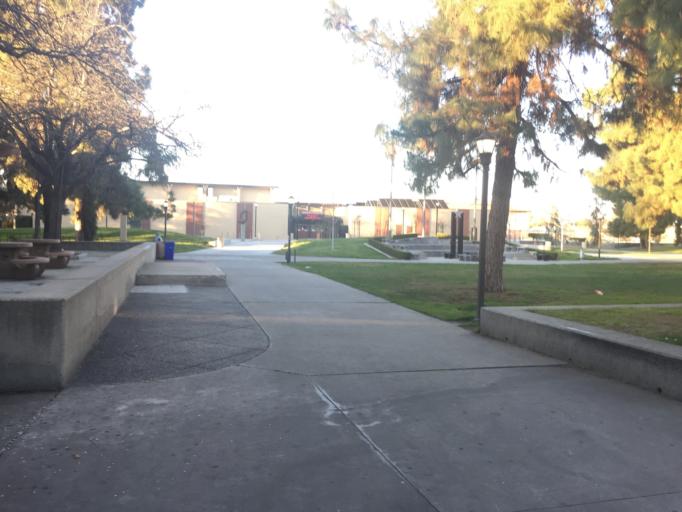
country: US
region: California
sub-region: Fresno County
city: Fresno
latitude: 36.7680
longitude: -119.7968
